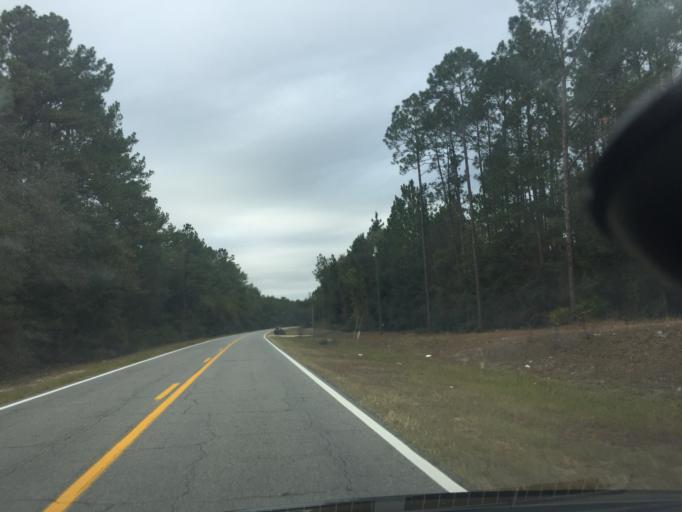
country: US
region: Georgia
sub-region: Chatham County
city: Bloomingdale
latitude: 32.0968
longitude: -81.3790
